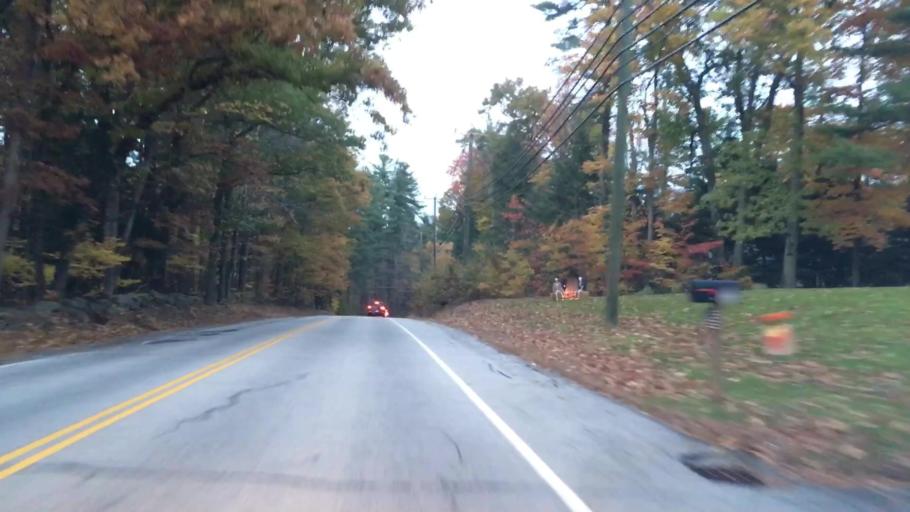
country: US
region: New Hampshire
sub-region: Hillsborough County
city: Milford
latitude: 42.8570
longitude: -71.6348
